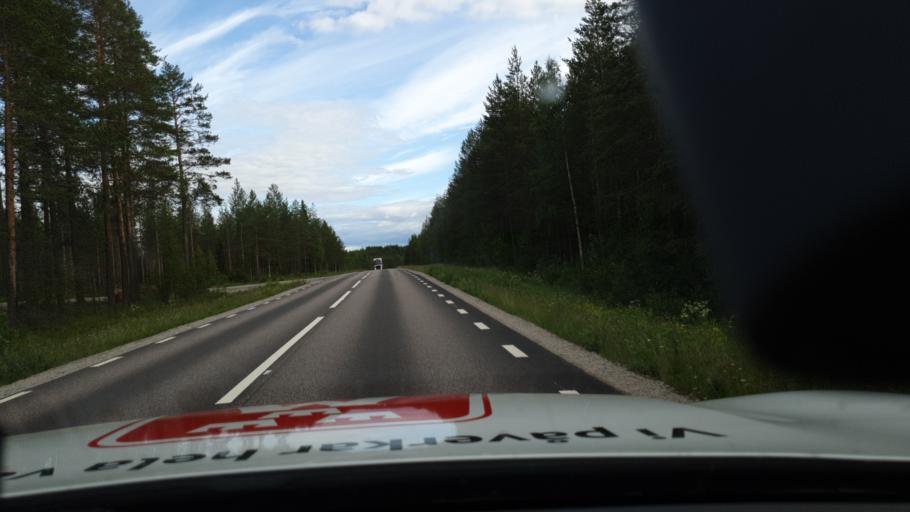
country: SE
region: Norrbotten
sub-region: Overkalix Kommun
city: OEverkalix
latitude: 66.3782
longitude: 22.8359
